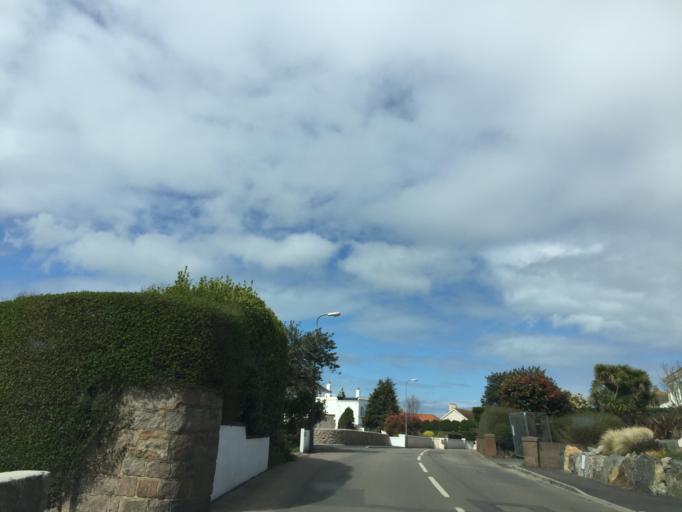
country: JE
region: St Helier
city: Saint Helier
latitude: 49.1802
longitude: -2.1759
